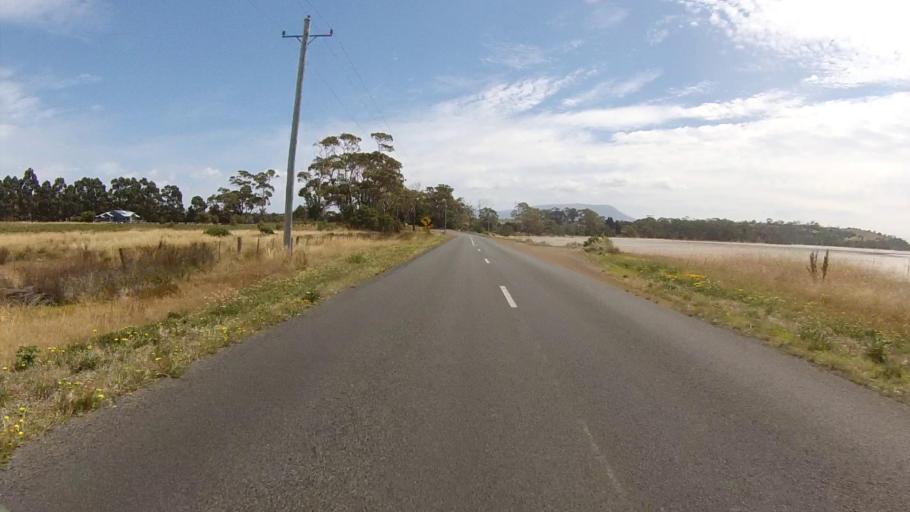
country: AU
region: Tasmania
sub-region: Clarence
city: Sandford
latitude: -43.0291
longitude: 147.4337
